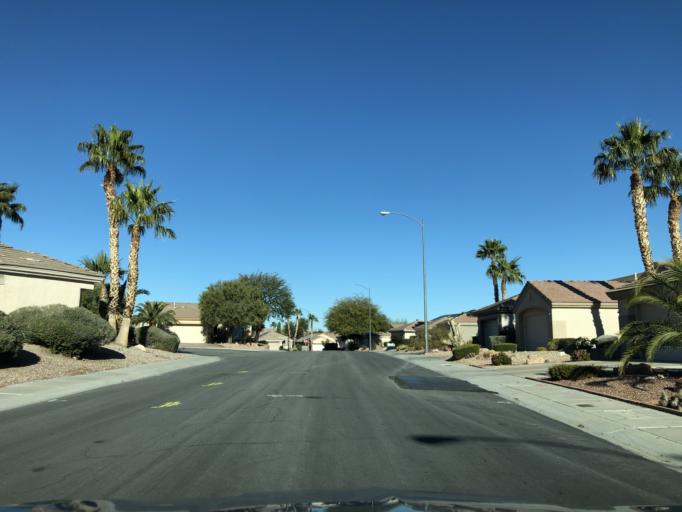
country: US
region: Nevada
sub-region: Clark County
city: Whitney
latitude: 36.0074
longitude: -115.0727
